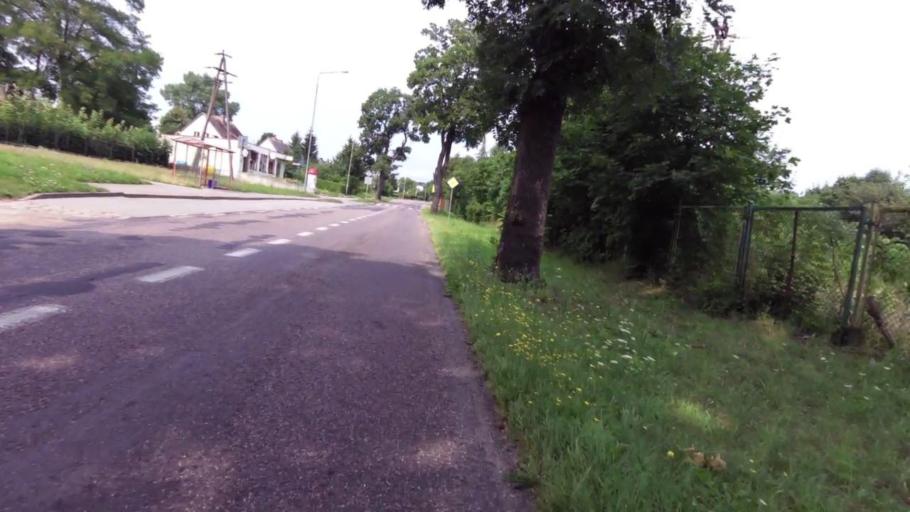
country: PL
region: West Pomeranian Voivodeship
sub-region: Powiat drawski
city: Drawsko Pomorskie
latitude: 53.5510
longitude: 15.8227
